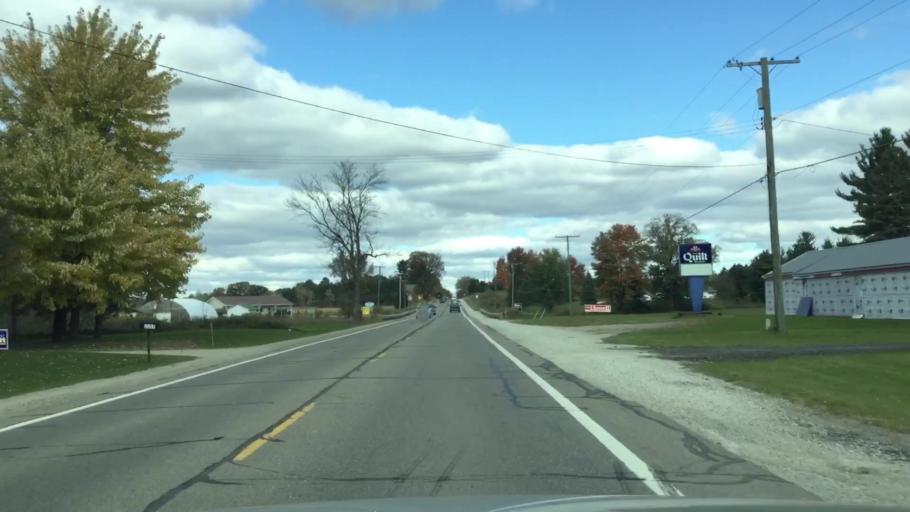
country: US
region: Michigan
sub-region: Lapeer County
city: Lapeer
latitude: 43.0948
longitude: -83.3079
